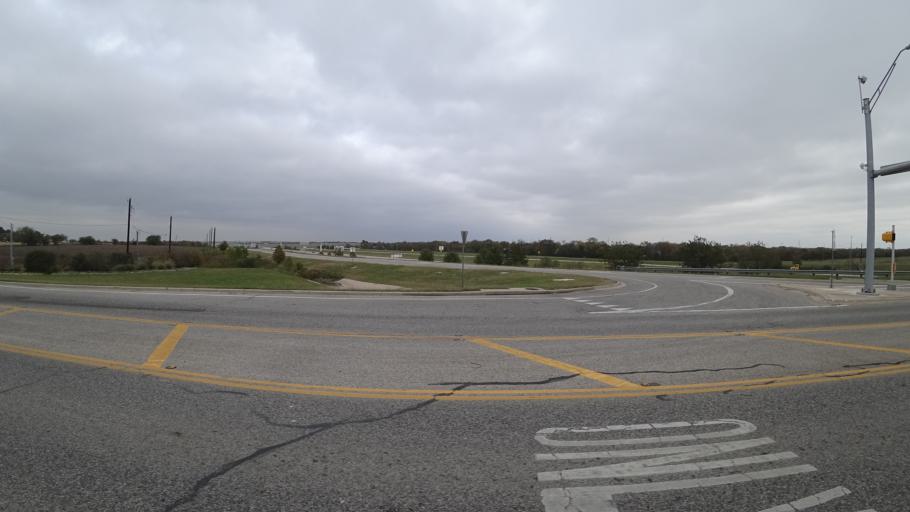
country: US
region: Texas
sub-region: Travis County
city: Pflugerville
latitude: 30.4242
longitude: -97.5894
